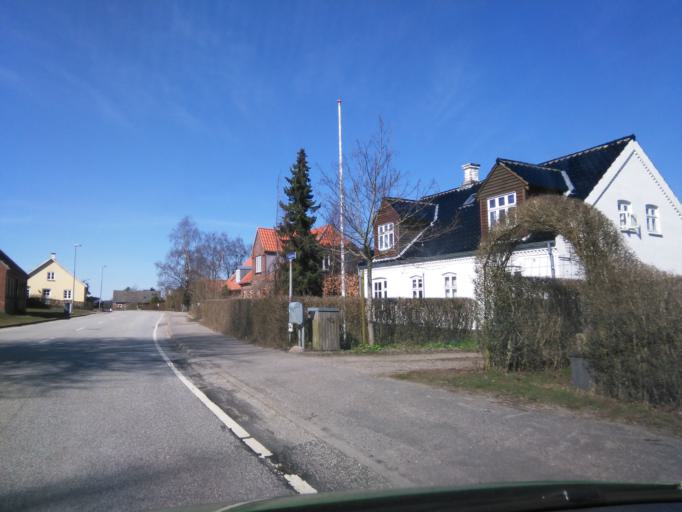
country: DK
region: Central Jutland
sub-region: Horsens Kommune
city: Braedstrup
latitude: 56.0204
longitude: 9.6456
